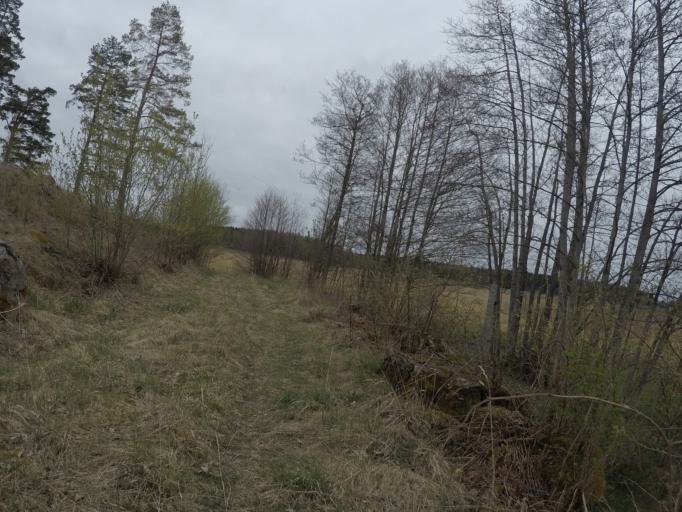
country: SE
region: Soedermanland
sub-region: Eskilstuna Kommun
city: Kvicksund
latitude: 59.4250
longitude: 16.2687
